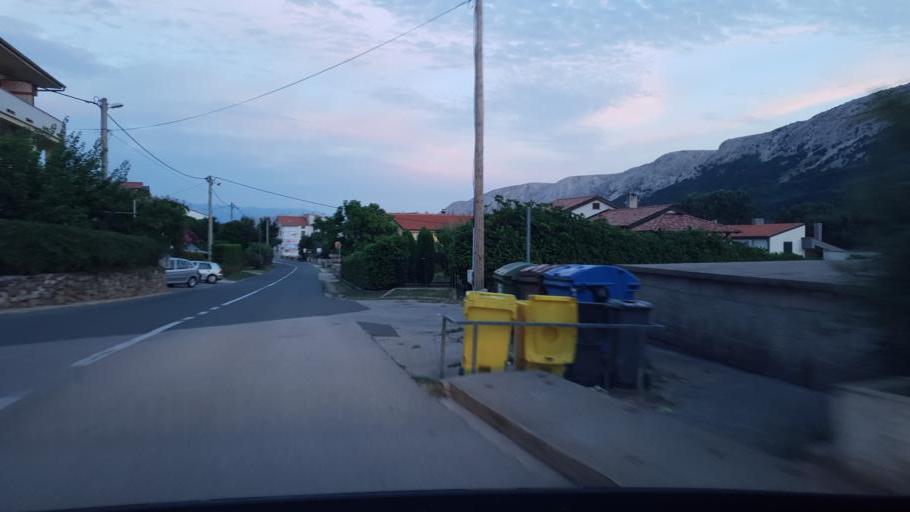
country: HR
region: Primorsko-Goranska
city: Punat
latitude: 44.9776
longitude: 14.7351
